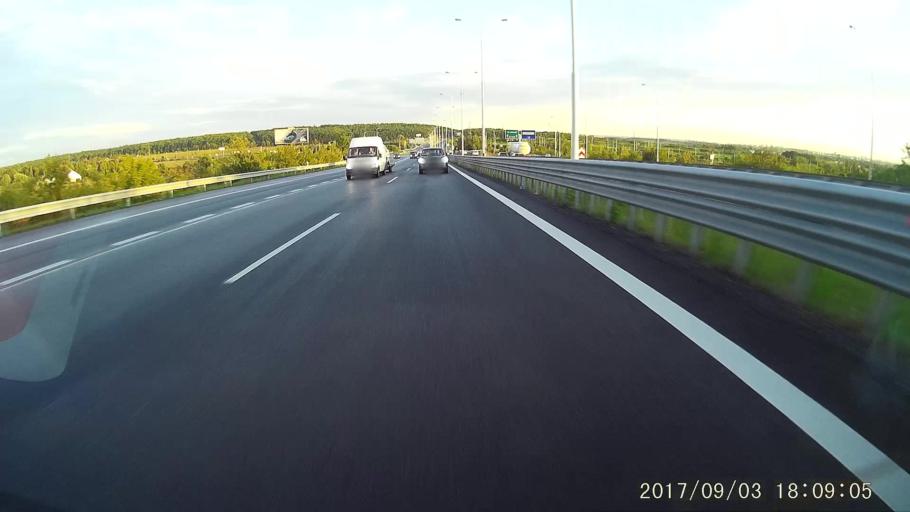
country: CZ
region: Praha
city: Cerny Most
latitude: 50.1040
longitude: 14.5900
